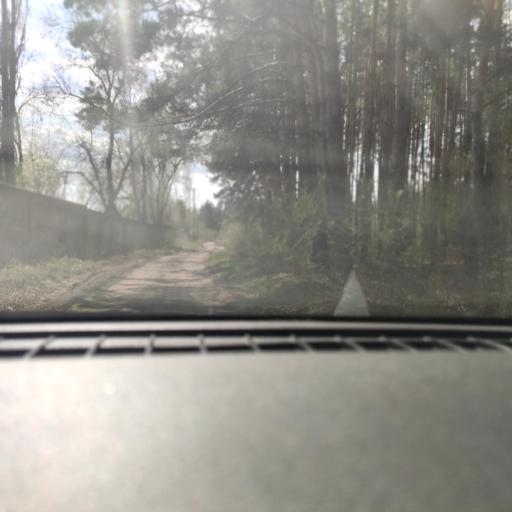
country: RU
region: Voronezj
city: Maslovka
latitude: 51.5963
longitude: 39.2183
